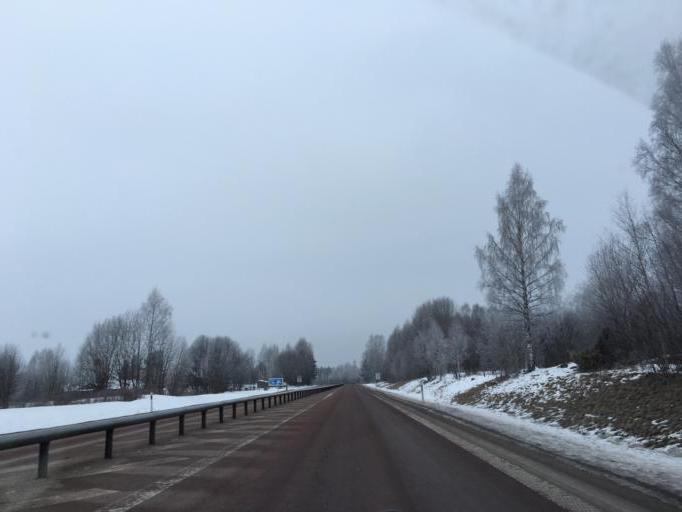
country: SE
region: Dalarna
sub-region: Mora Kommun
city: Mora
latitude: 61.0036
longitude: 14.6343
